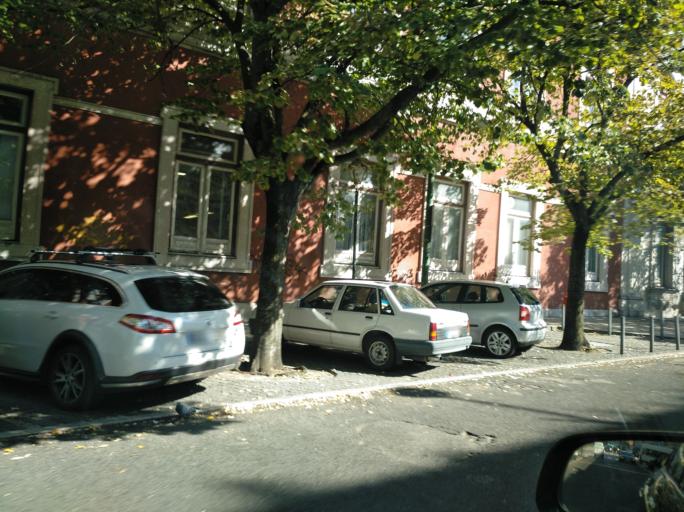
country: PT
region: Lisbon
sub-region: Lisbon
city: Lisbon
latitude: 38.7198
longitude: -9.1399
